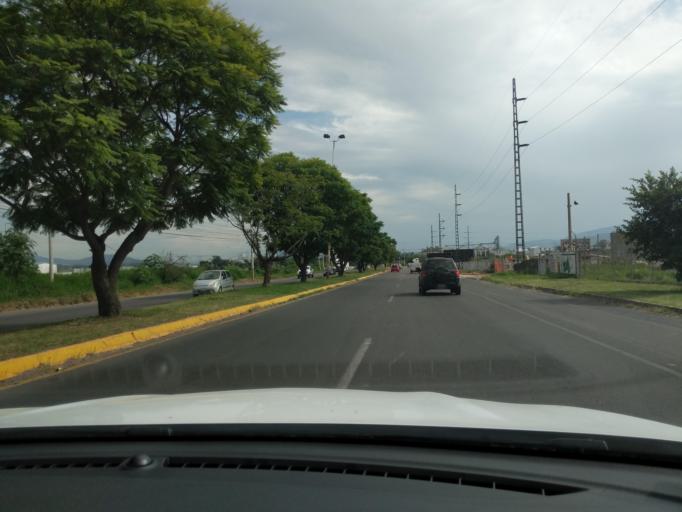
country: MX
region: Jalisco
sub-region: El Salto
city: El Muey
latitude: 20.5008
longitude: -103.2314
